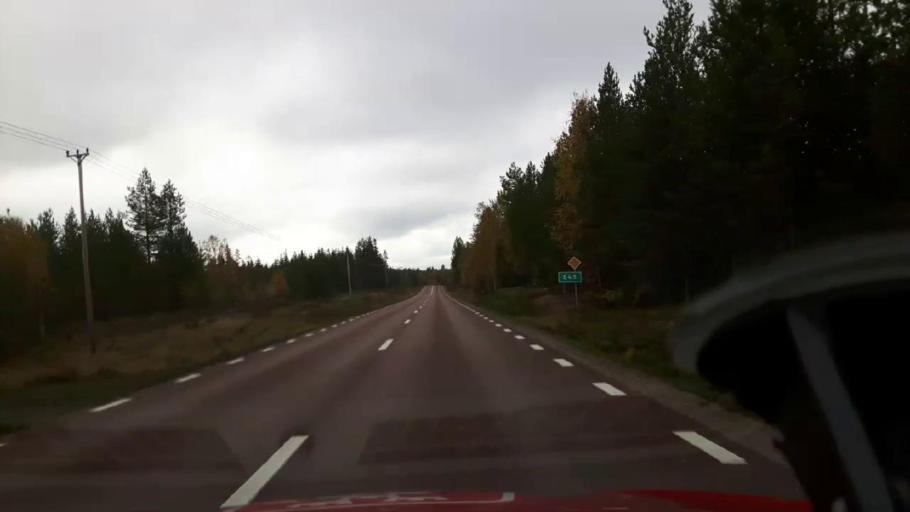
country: SE
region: Jaemtland
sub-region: Harjedalens Kommun
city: Sveg
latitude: 62.2273
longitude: 14.8449
